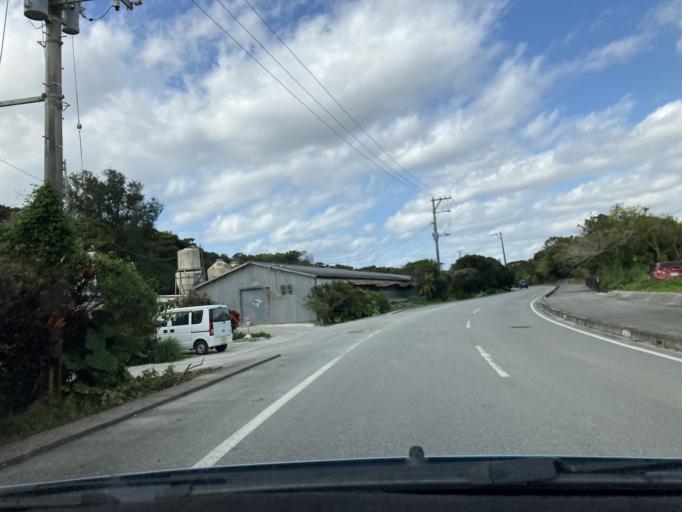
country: JP
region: Okinawa
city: Tomigusuku
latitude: 26.1773
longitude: 127.7609
